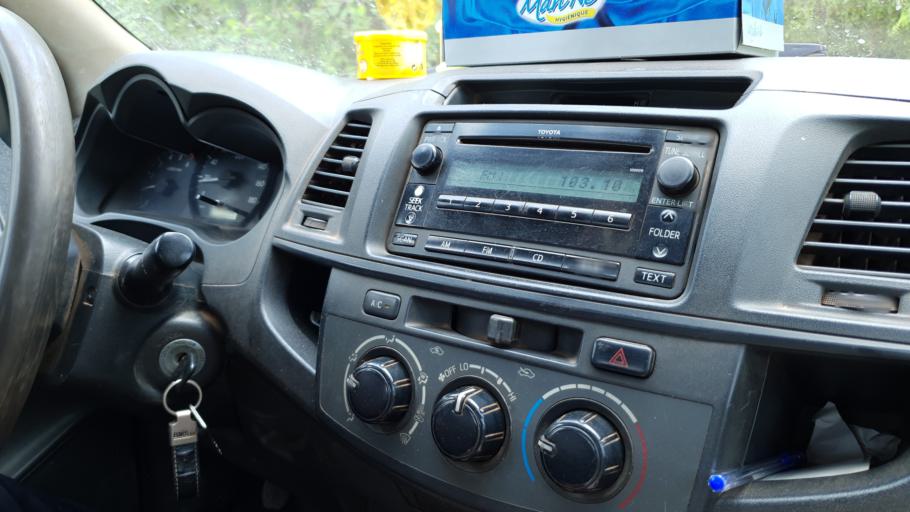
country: ML
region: Segou
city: Baroueli
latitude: 13.3533
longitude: -7.0967
